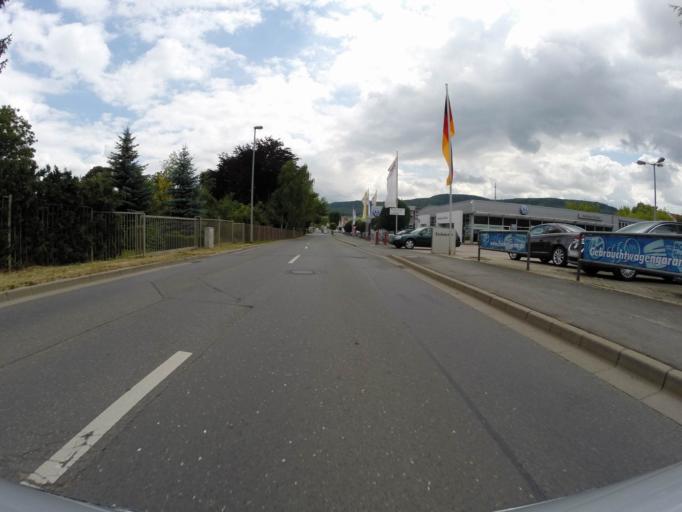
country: DE
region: Thuringia
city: Jena
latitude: 50.9574
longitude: 11.6180
